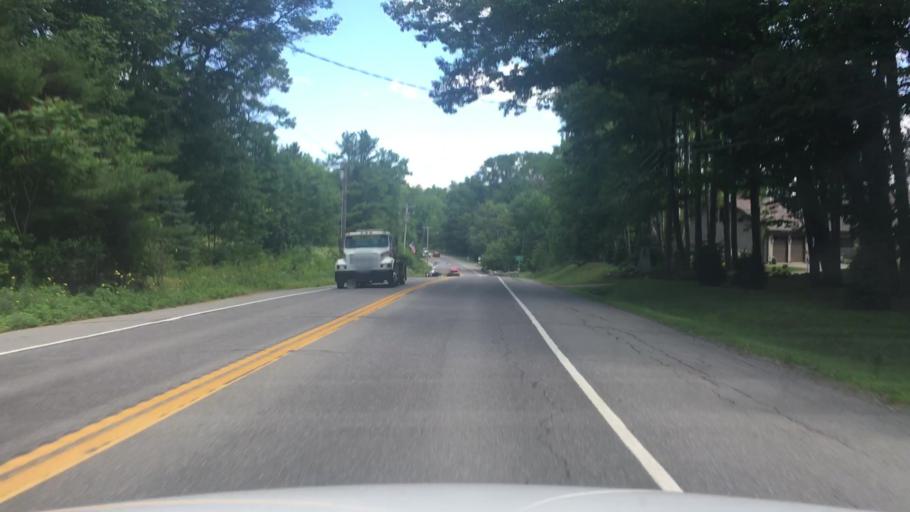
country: US
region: Maine
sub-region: Waldo County
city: Belfast
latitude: 44.3931
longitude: -68.9899
